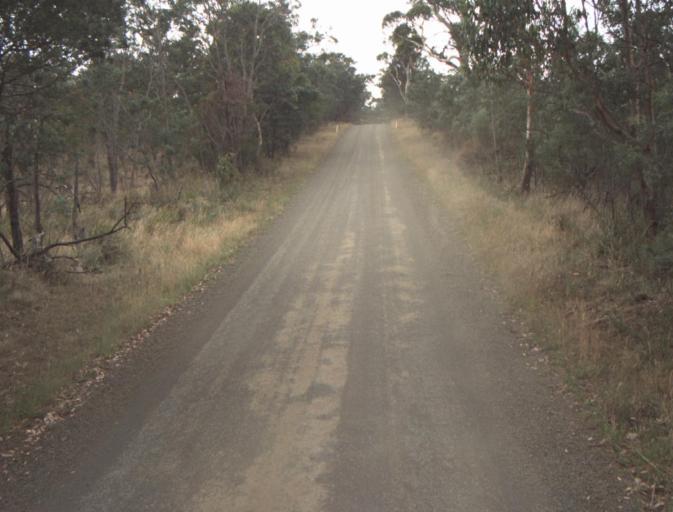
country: AU
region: Tasmania
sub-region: Northern Midlands
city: Evandale
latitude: -41.5287
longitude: 147.3574
